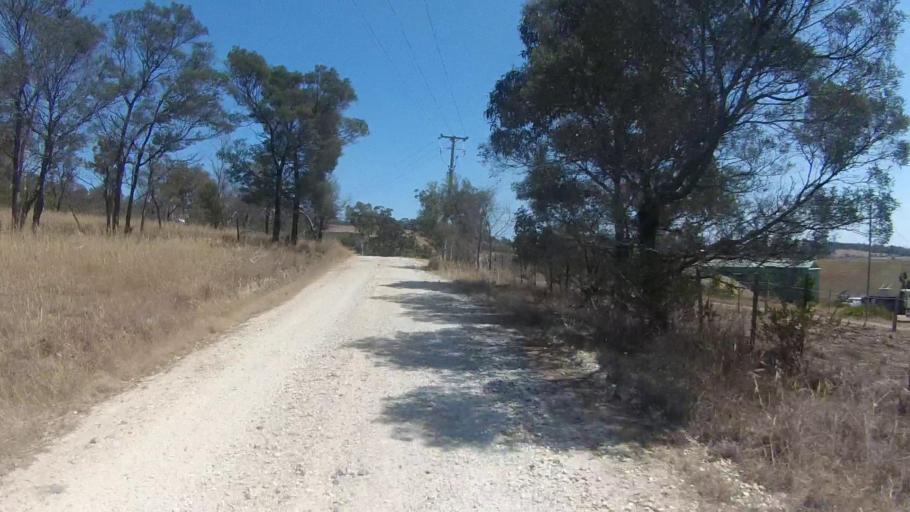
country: AU
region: Tasmania
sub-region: Sorell
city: Sorell
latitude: -42.8274
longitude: 147.6582
